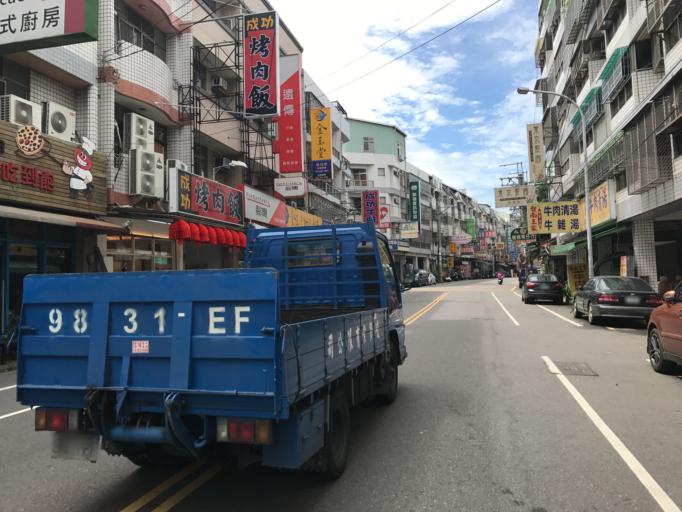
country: TW
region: Taiwan
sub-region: Taichung City
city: Taichung
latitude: 24.0934
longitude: 120.7037
